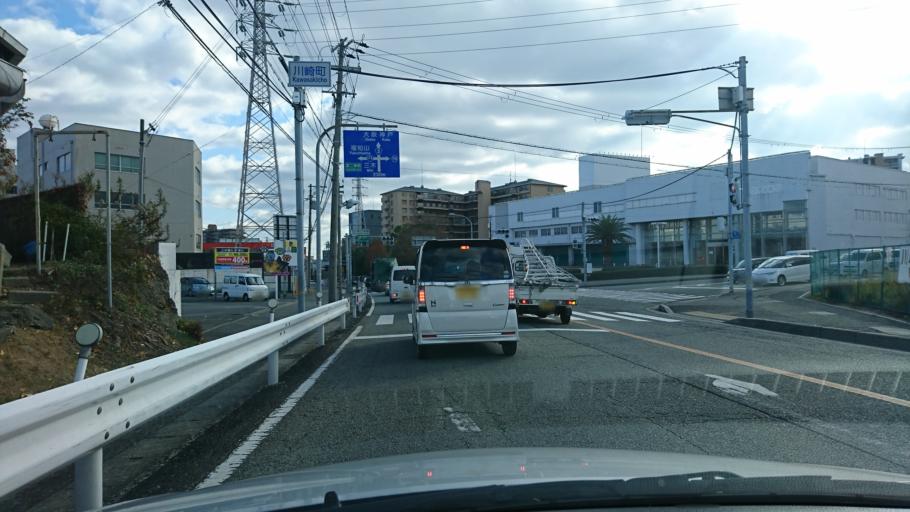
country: JP
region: Hyogo
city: Akashi
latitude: 34.6560
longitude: 134.9731
